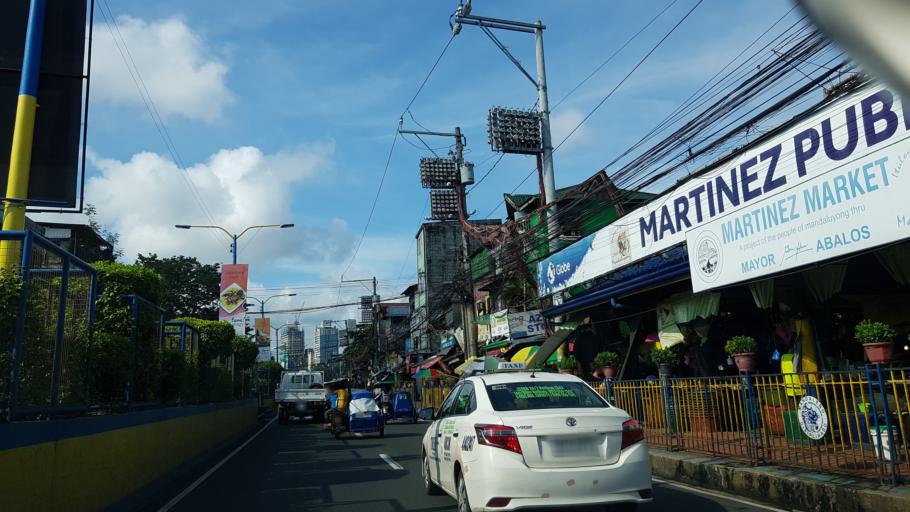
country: PH
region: Metro Manila
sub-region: Mandaluyong
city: Mandaluyong City
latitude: 14.5809
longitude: 121.0365
